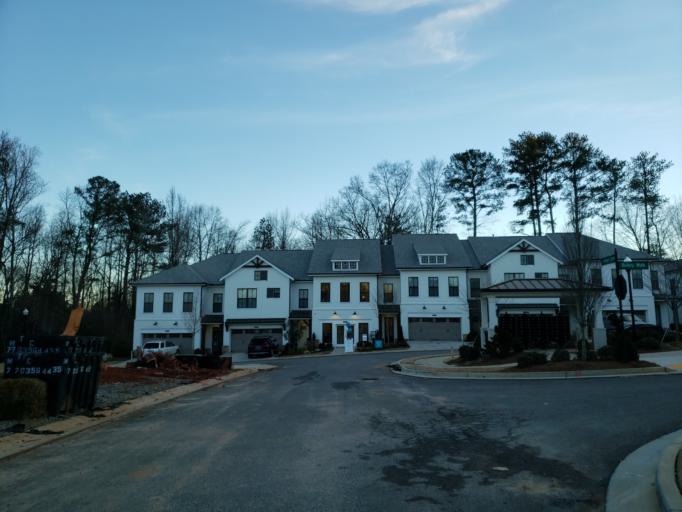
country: US
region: Georgia
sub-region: Fulton County
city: Alpharetta
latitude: 34.0693
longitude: -84.2890
